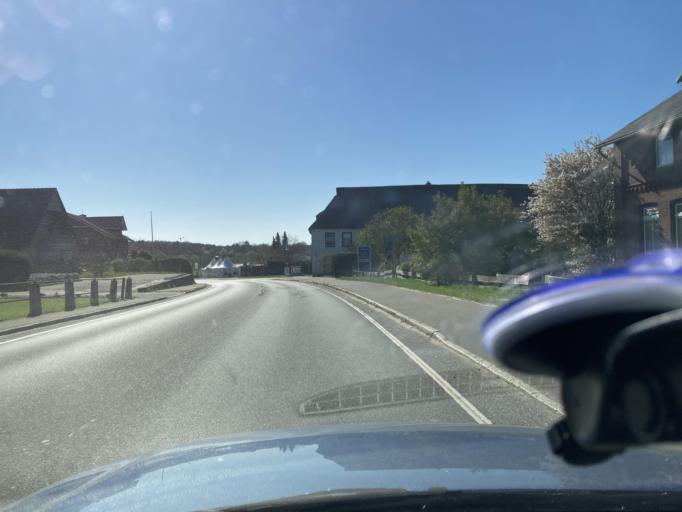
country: DE
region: Schleswig-Holstein
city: Nordhastedt
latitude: 54.1767
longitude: 9.1823
